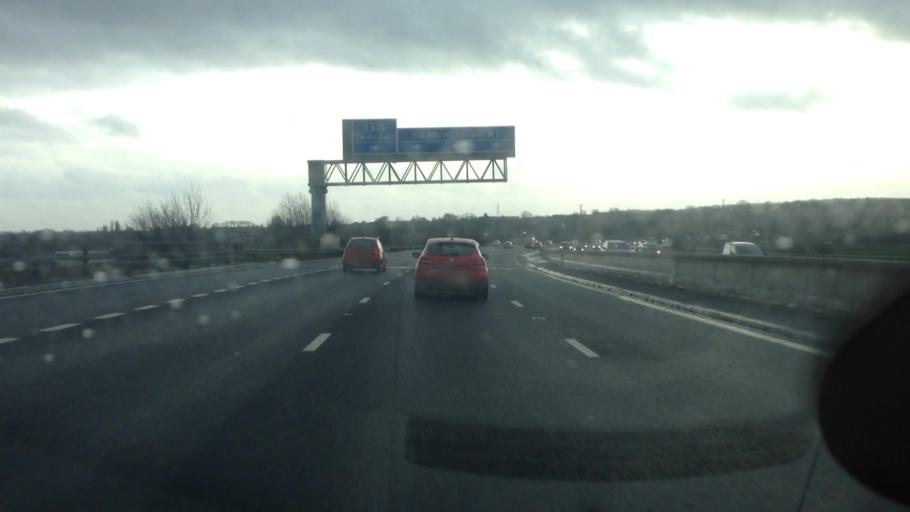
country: GB
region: England
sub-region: City and Borough of Wakefield
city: Crigglestone
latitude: 53.6563
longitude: -1.5287
